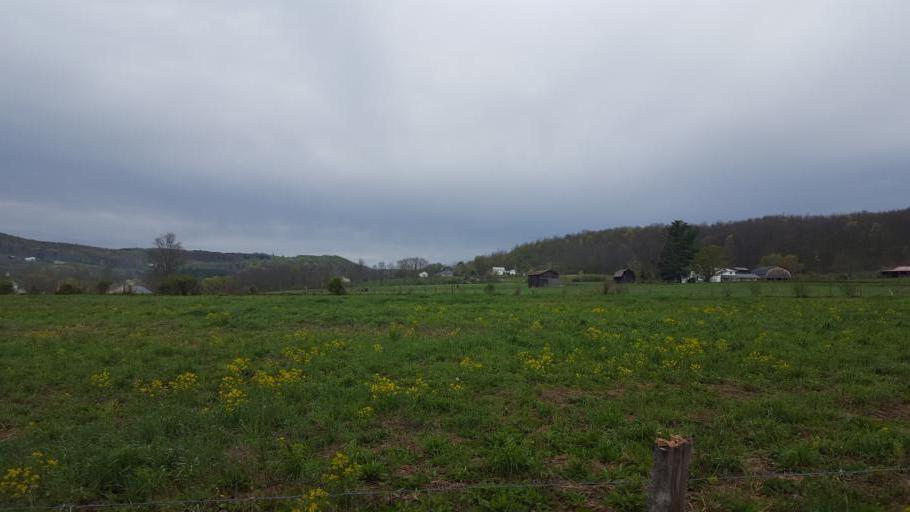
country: US
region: Pennsylvania
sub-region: Tioga County
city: Elkland
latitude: 42.0808
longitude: -77.4485
